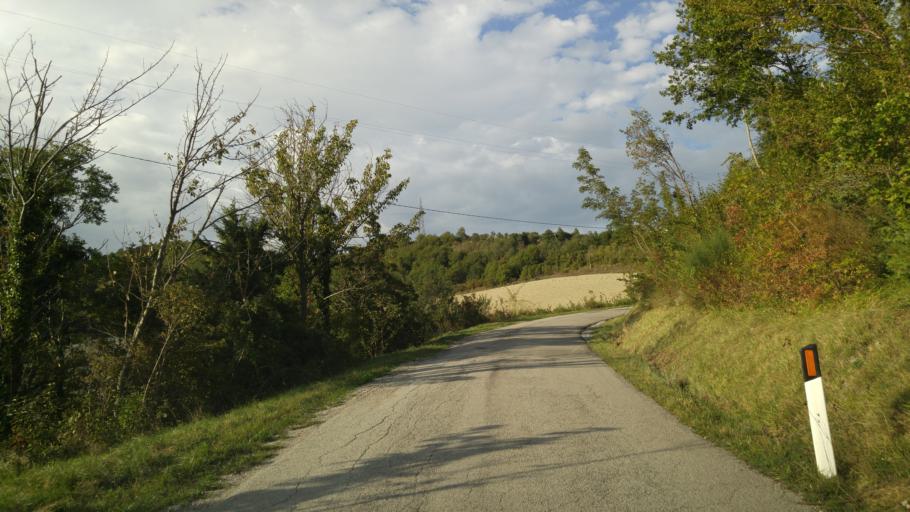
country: IT
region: The Marches
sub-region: Provincia di Pesaro e Urbino
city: Cagli
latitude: 43.5579
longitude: 12.6301
